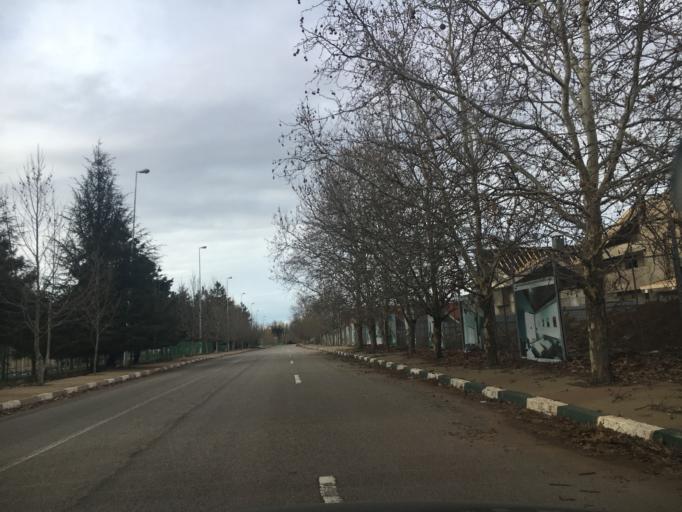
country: MA
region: Meknes-Tafilalet
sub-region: Ifrane
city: Ifrane
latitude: 33.5263
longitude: -5.1329
